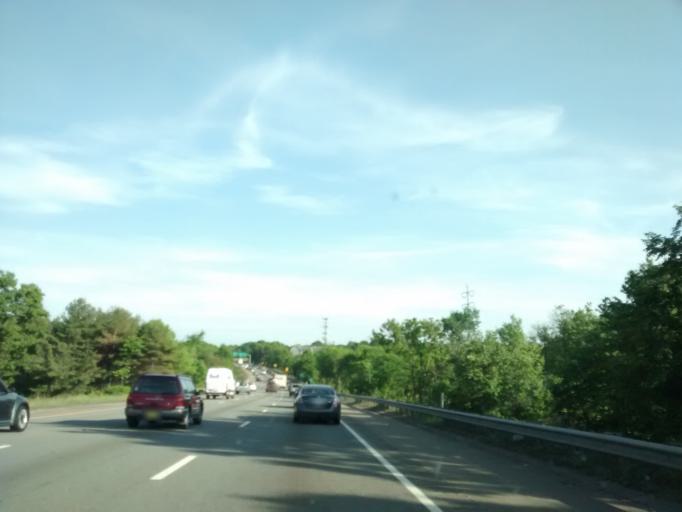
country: US
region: Massachusetts
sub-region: Middlesex County
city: Hudson
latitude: 42.3703
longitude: -71.5964
